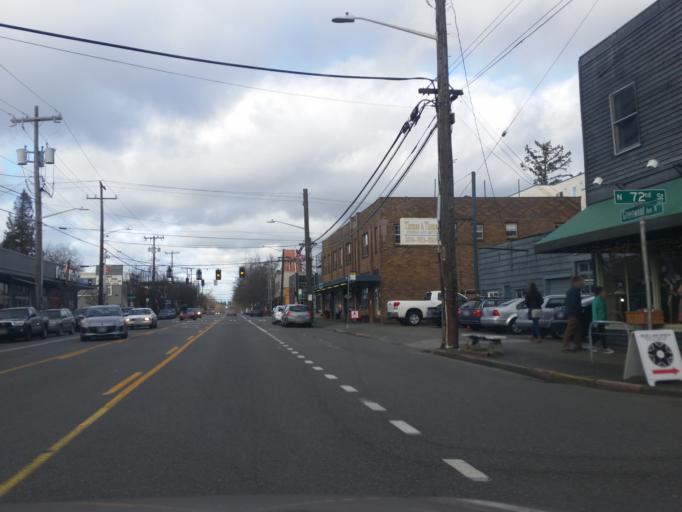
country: US
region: Washington
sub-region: King County
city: Shoreline
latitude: 47.6811
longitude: -122.3553
